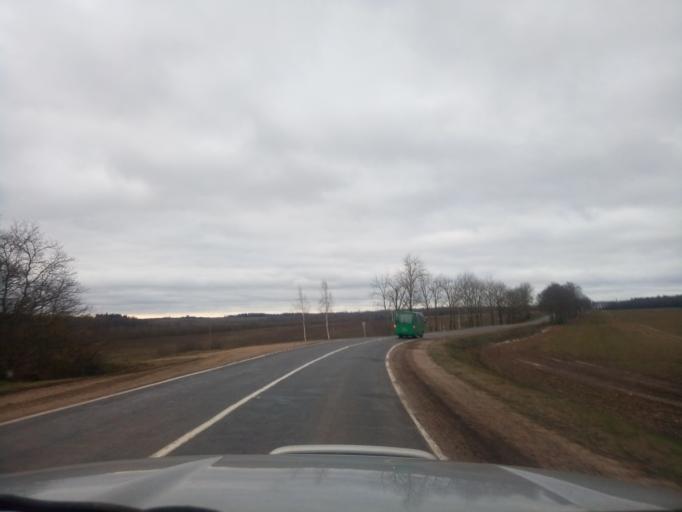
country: BY
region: Minsk
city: Kapyl'
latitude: 53.1722
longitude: 27.1596
